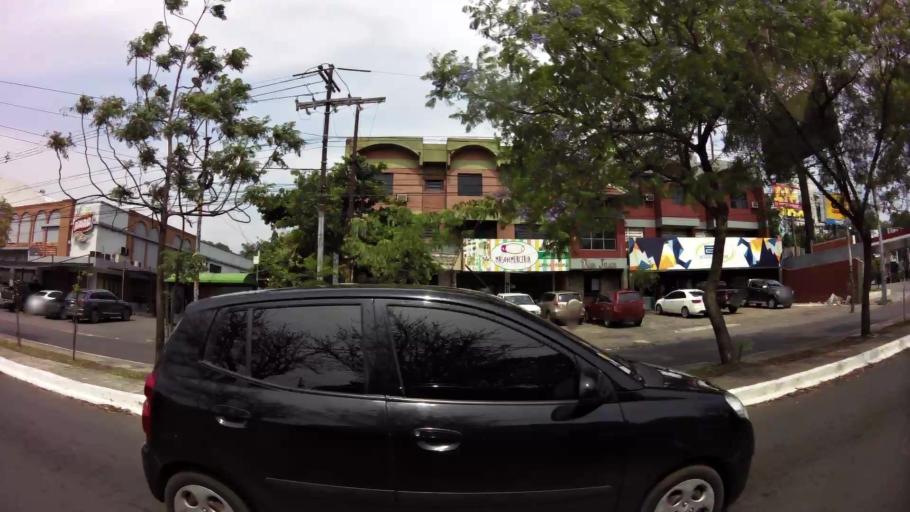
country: PY
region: Asuncion
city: Asuncion
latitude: -25.2947
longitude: -57.5767
